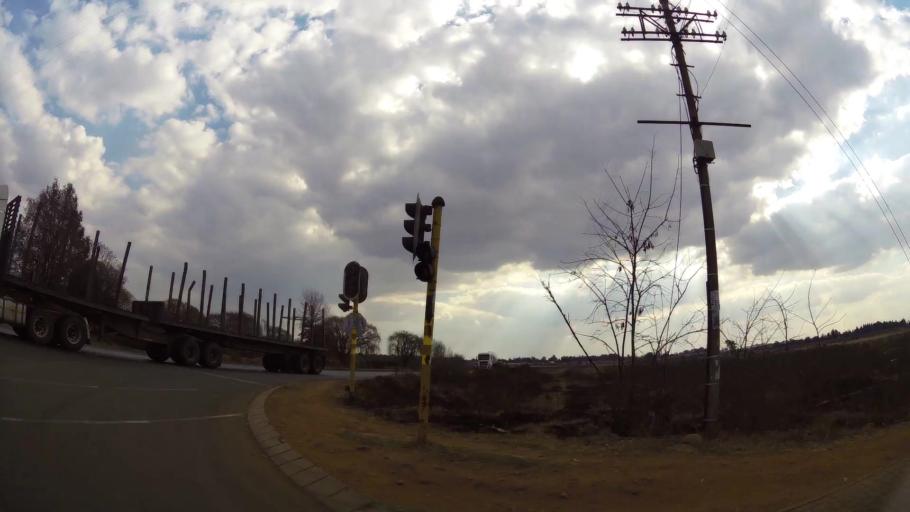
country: ZA
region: Mpumalanga
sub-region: Nkangala District Municipality
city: Delmas
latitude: -26.1439
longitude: 28.6873
